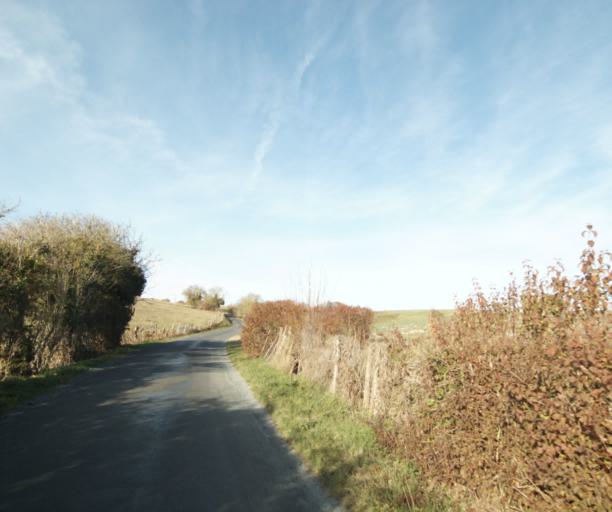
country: FR
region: Poitou-Charentes
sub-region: Departement de la Charente-Maritime
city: Chaniers
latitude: 45.7300
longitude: -0.5865
